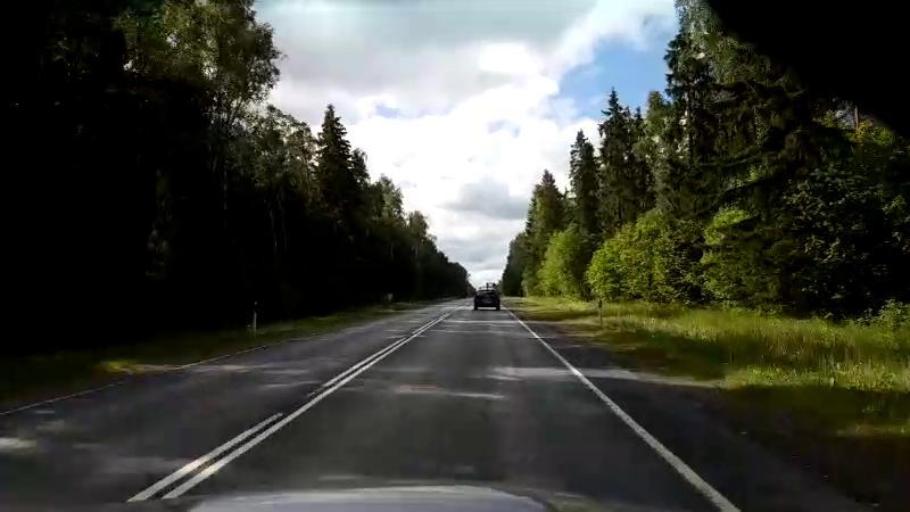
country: EE
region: Harju
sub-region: Saue linn
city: Saue
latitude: 59.2064
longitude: 24.4970
